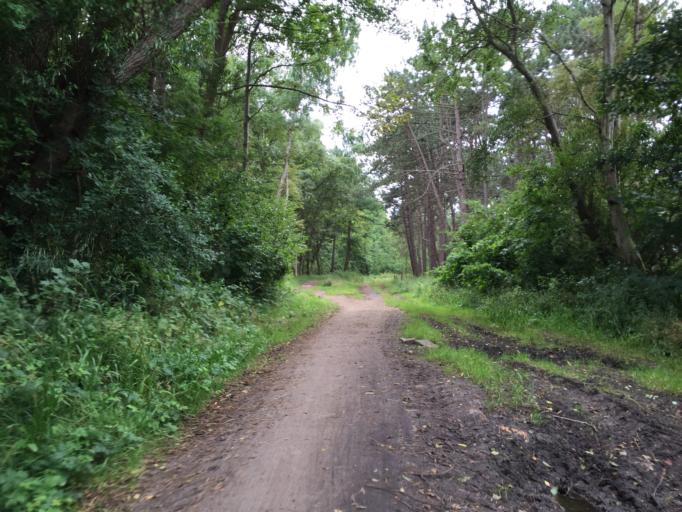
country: DE
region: Mecklenburg-Vorpommern
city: Hiddensee
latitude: 54.5171
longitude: 13.0812
